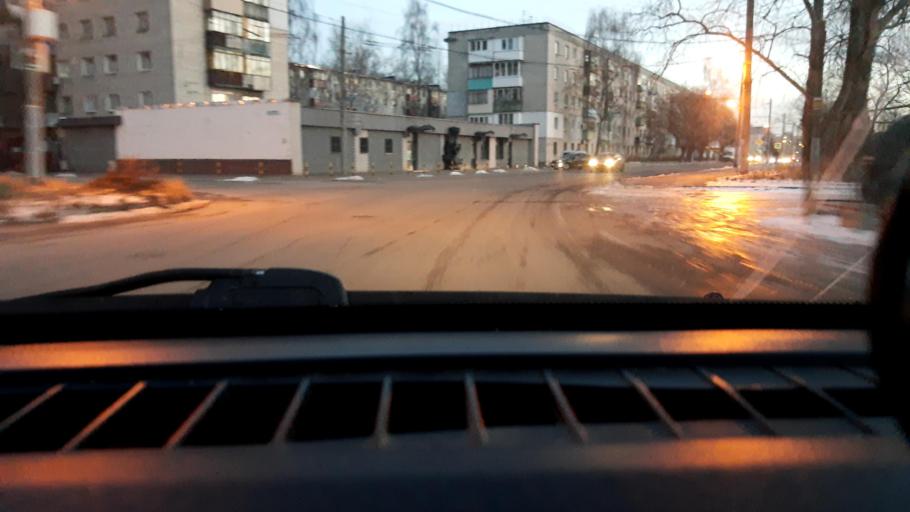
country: RU
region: Nizjnij Novgorod
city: Gorbatovka
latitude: 56.2851
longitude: 43.8479
